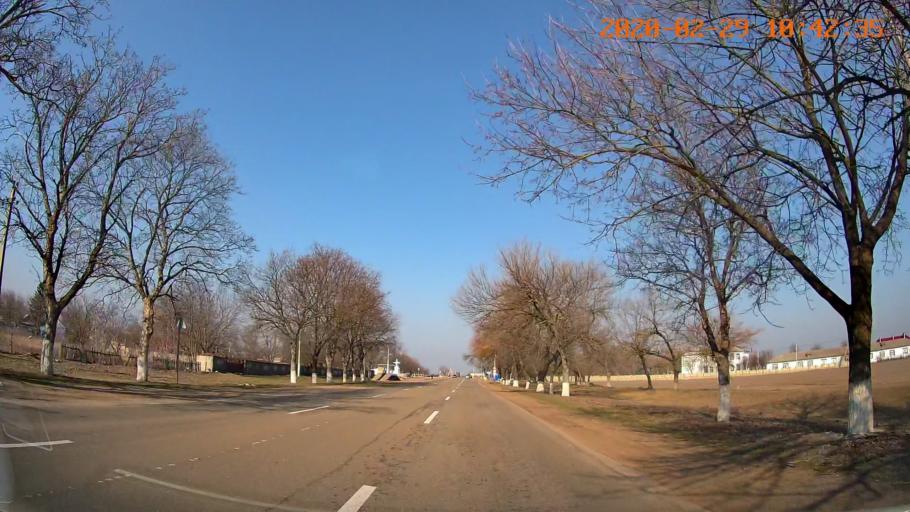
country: MD
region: Telenesti
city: Grigoriopol
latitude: 47.0529
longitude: 29.4091
